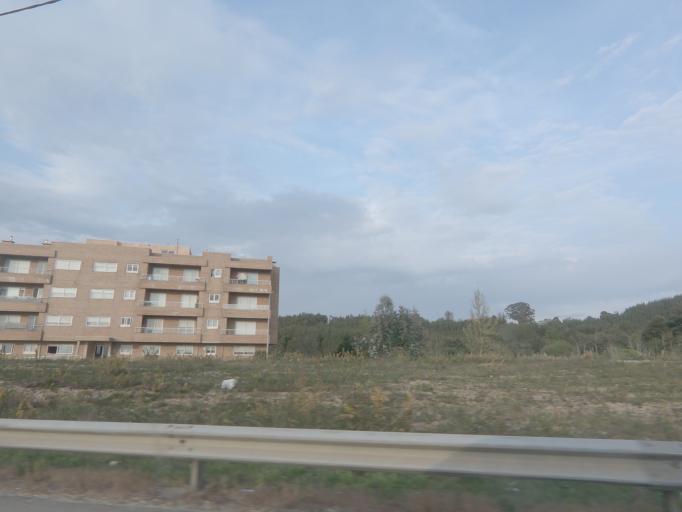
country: PT
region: Porto
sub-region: Gondomar
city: Baguim do Monte
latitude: 41.2039
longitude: -8.5274
